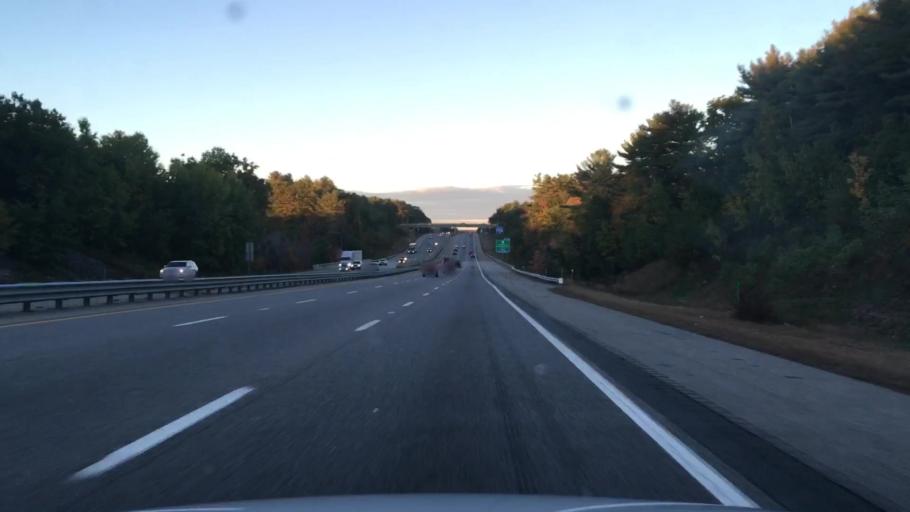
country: US
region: Maine
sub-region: York County
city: West Kennebunk
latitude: 43.3981
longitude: -70.5663
